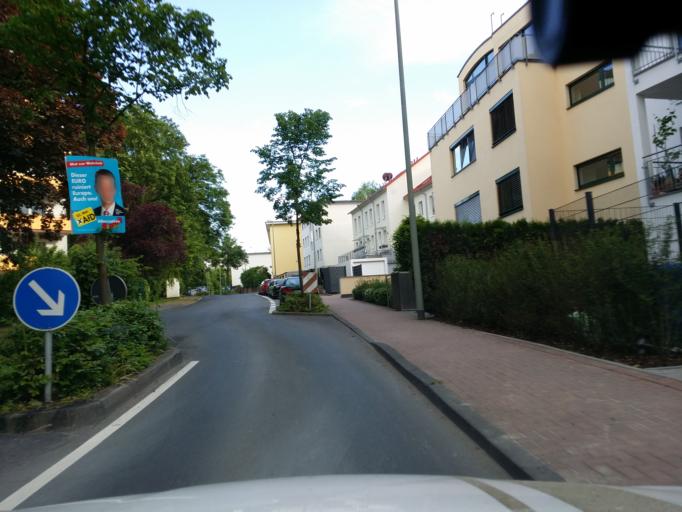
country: DE
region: Hesse
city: Kelkheim (Taunus)
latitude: 50.1370
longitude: 8.4467
